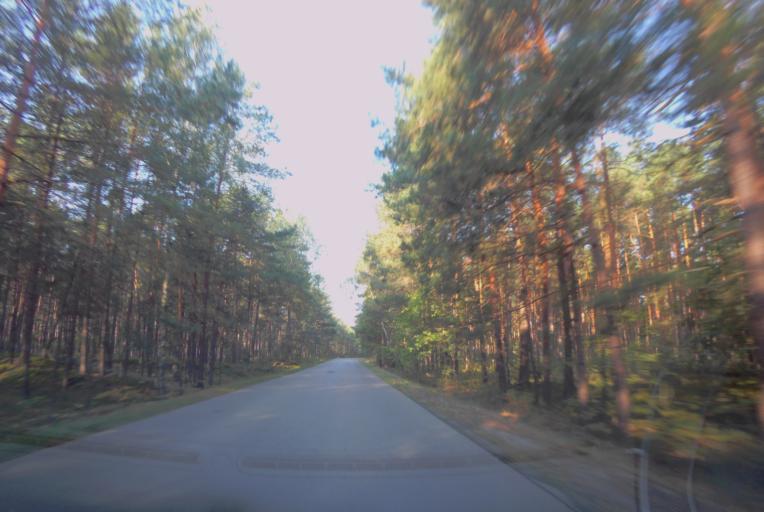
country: PL
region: Subcarpathian Voivodeship
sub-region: Powiat nizanski
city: Harasiuki
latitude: 50.5092
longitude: 22.4218
